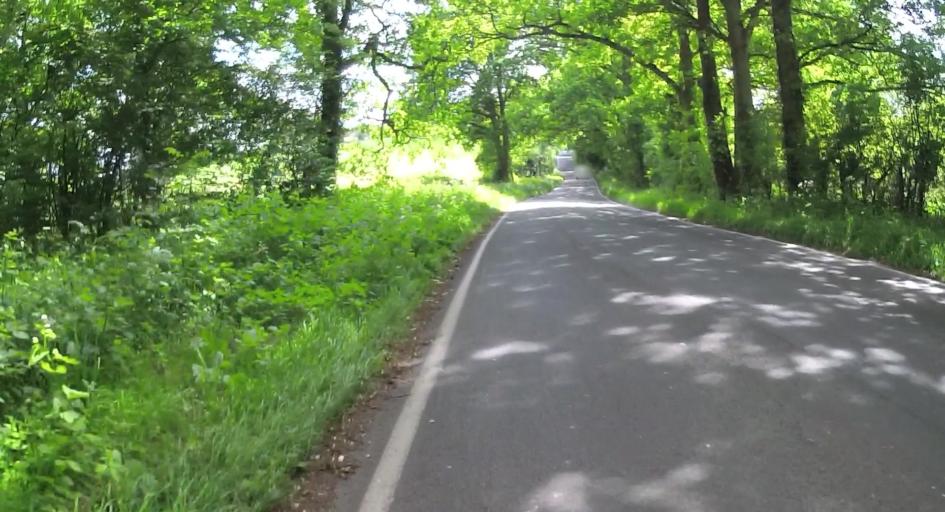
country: GB
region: England
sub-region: Surrey
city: Farnham
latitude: 51.2235
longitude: -0.8387
